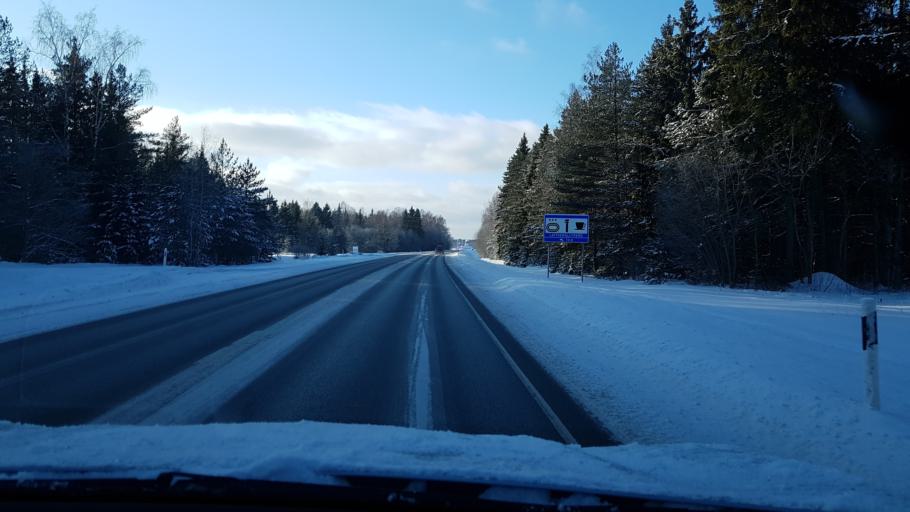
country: EE
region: Harju
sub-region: Nissi vald
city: Riisipere
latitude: 59.1802
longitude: 24.3788
